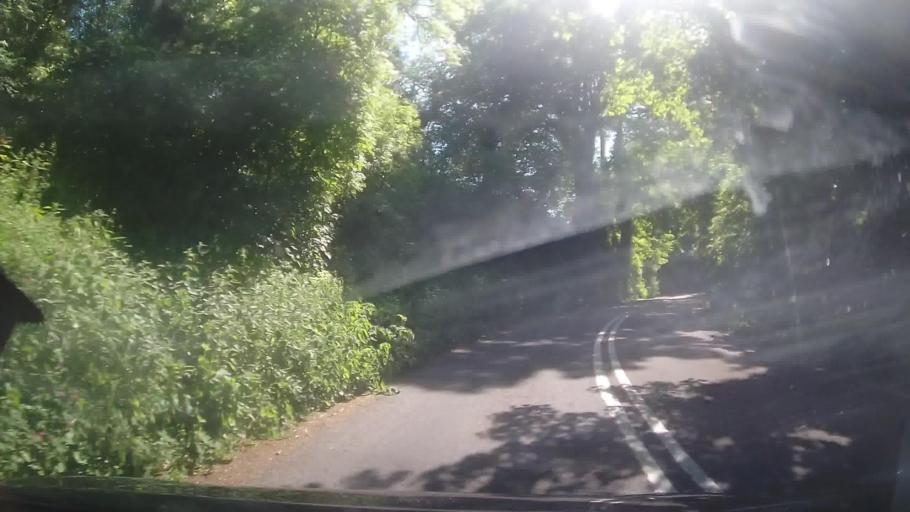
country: GB
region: England
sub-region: Devon
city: Dartmouth
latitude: 50.3641
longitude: -3.5723
